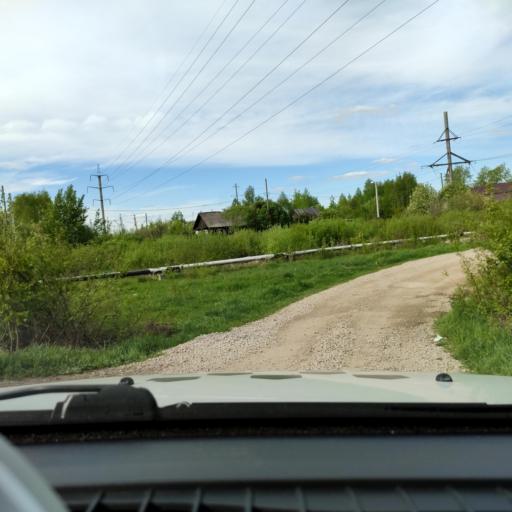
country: RU
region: Perm
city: Kondratovo
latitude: 58.0033
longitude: 56.1011
